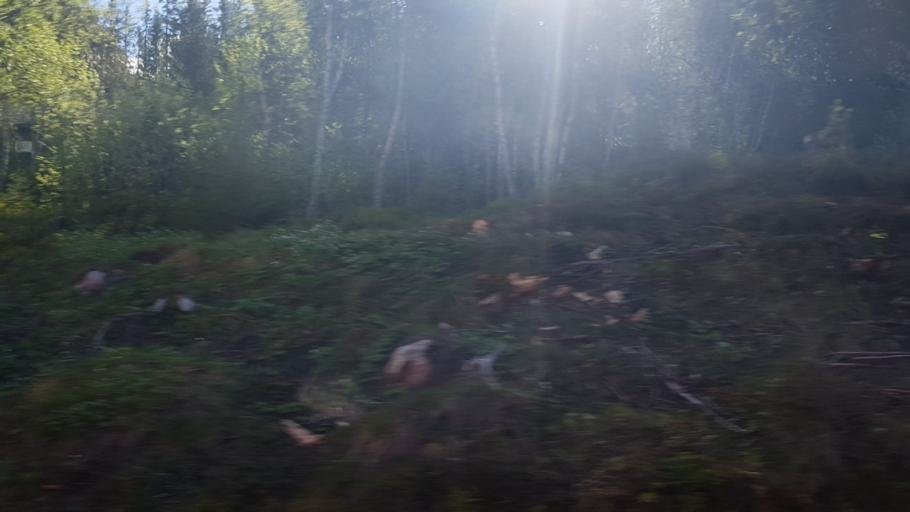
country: NO
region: Sor-Trondelag
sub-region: Rennebu
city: Berkak
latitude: 62.8342
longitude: 10.0171
